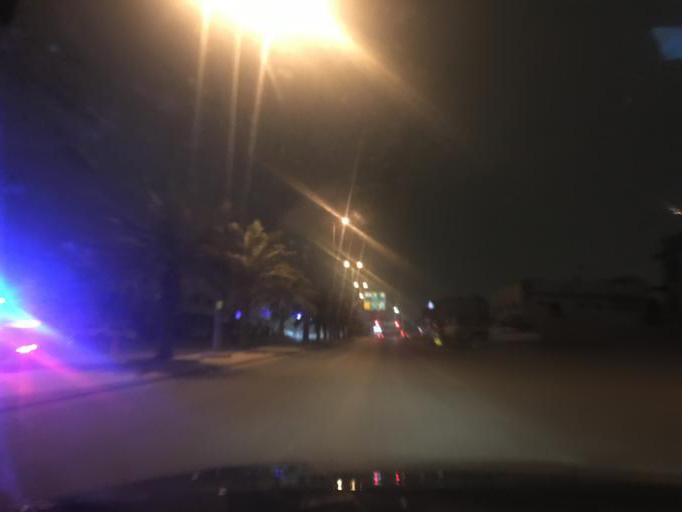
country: SA
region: Ar Riyad
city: Riyadh
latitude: 24.7489
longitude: 46.7771
